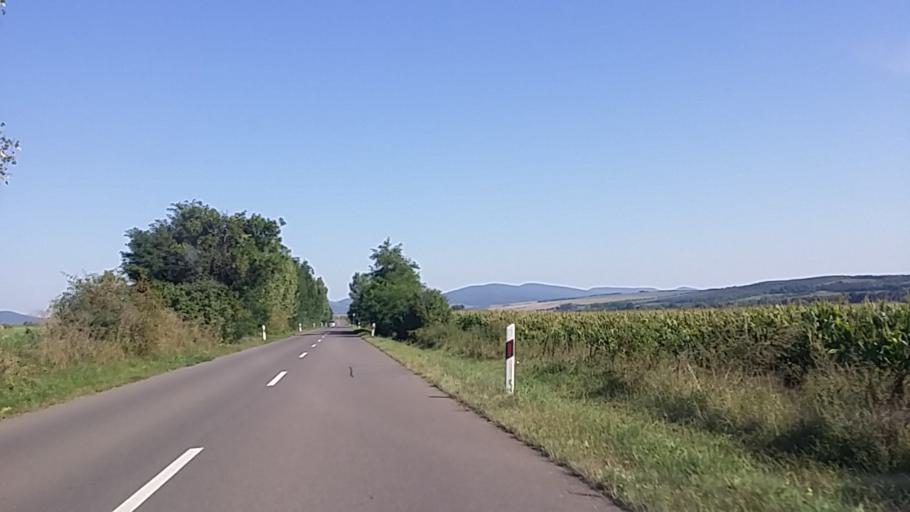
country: HU
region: Nograd
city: Jobbagyi
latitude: 47.8443
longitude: 19.6316
